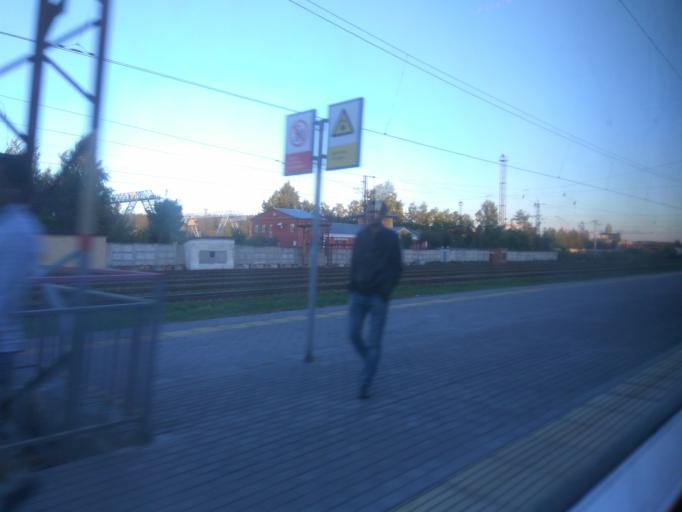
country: RU
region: Moskovskaya
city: Elektrostal'
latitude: 55.7697
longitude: 38.4684
